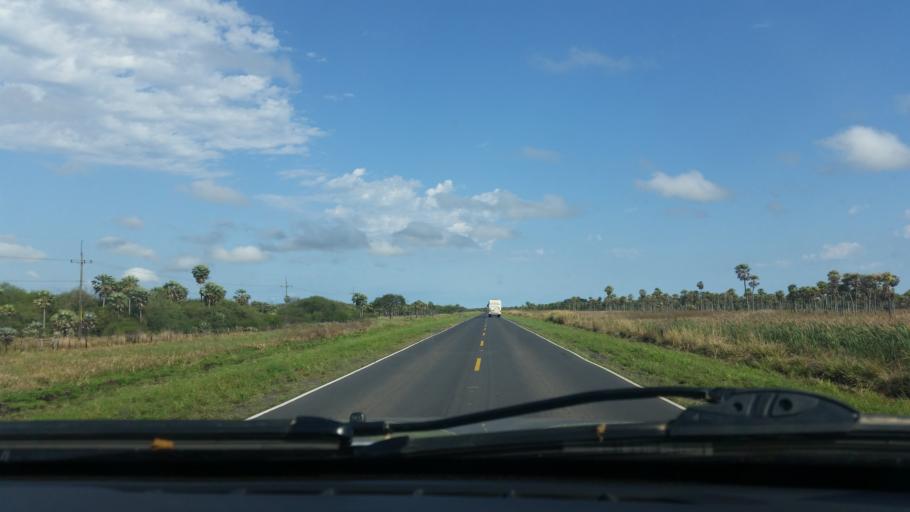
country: PY
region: Presidente Hayes
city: Benjamin Aceval
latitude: -24.9167
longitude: -57.6119
